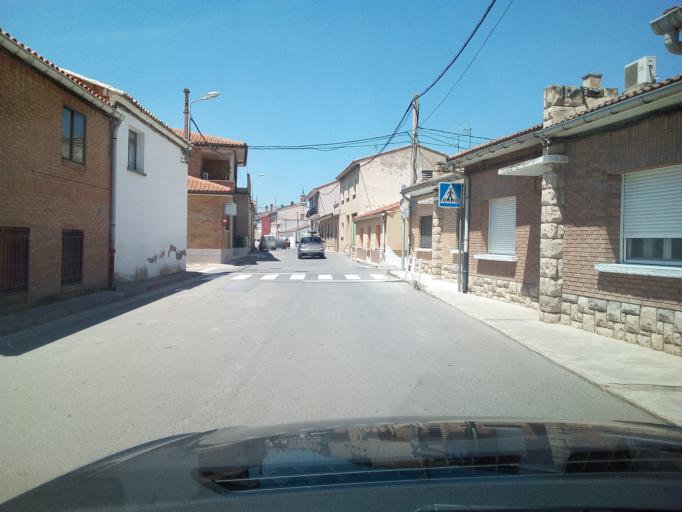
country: ES
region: Navarre
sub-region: Provincia de Navarra
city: Arguedas
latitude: 42.1738
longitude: -1.5935
